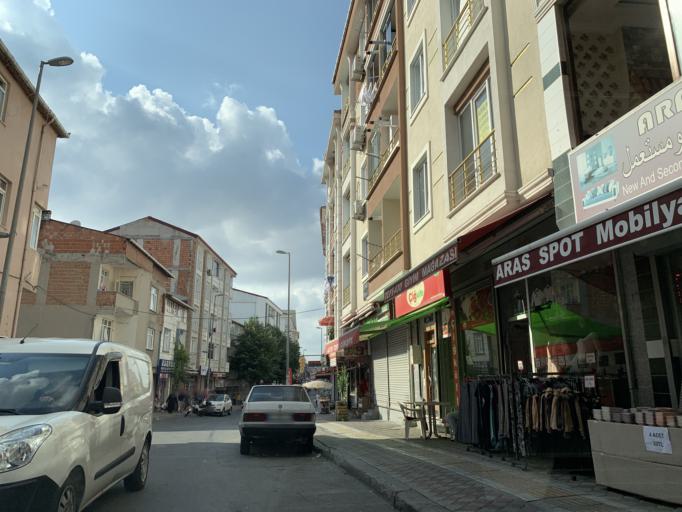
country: TR
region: Istanbul
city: Esenyurt
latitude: 41.0289
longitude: 28.6771
